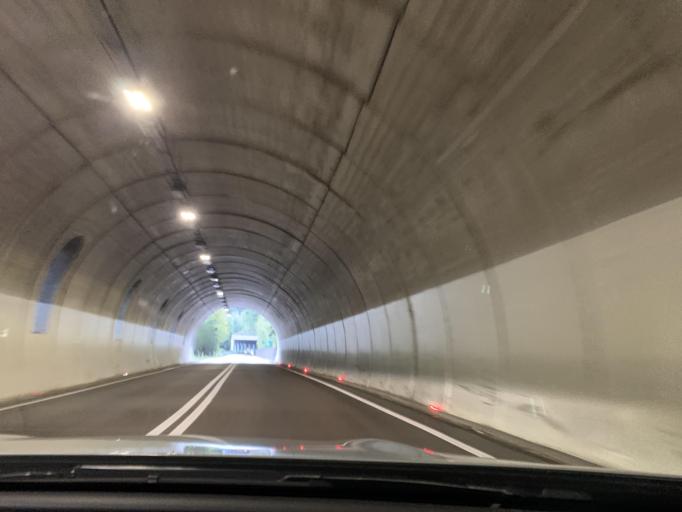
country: IT
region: Trentino-Alto Adige
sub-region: Bolzano
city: Nova Ponente
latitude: 46.4541
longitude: 11.4404
